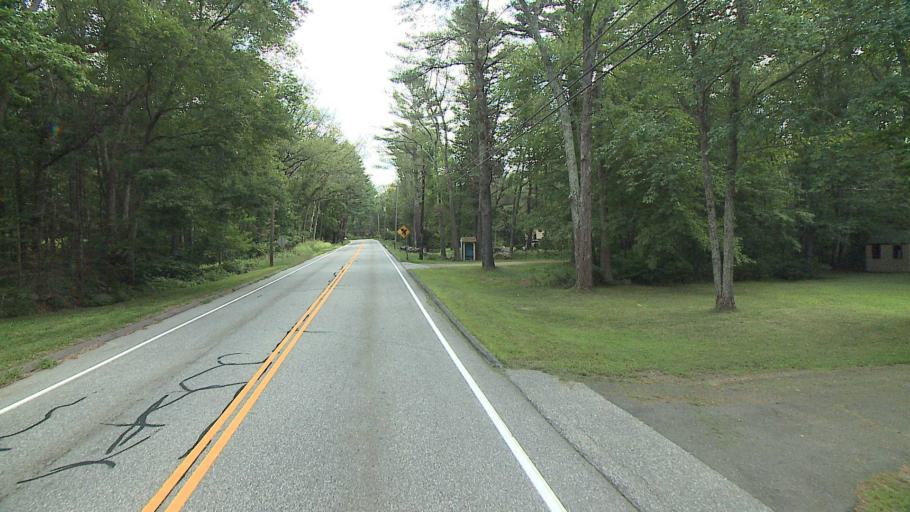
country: US
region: Connecticut
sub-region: Tolland County
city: Crystal Lake
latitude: 41.9193
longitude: -72.4166
